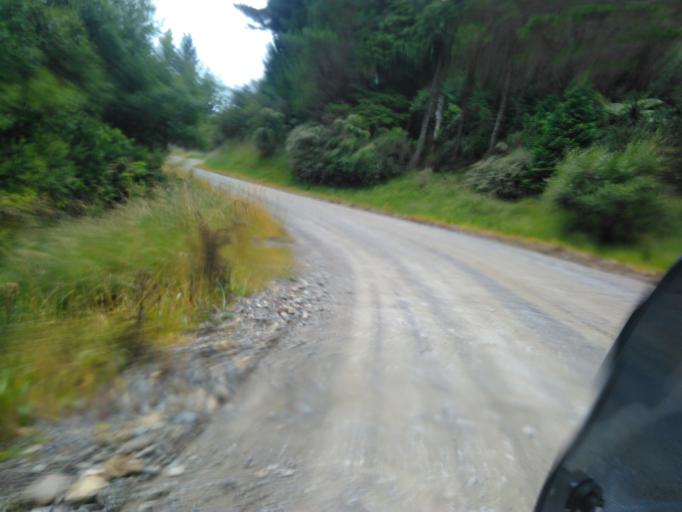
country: NZ
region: Gisborne
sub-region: Gisborne District
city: Gisborne
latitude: -38.0576
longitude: 178.1402
